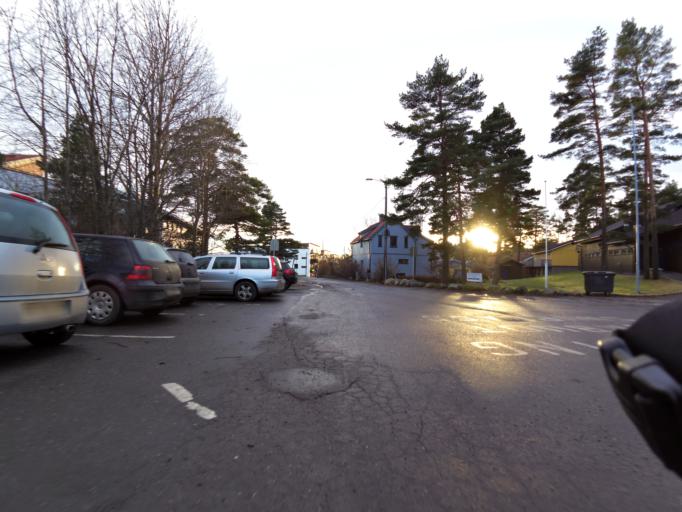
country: NO
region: Ostfold
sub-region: Fredrikstad
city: Fredrikstad
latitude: 59.2290
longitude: 10.9508
